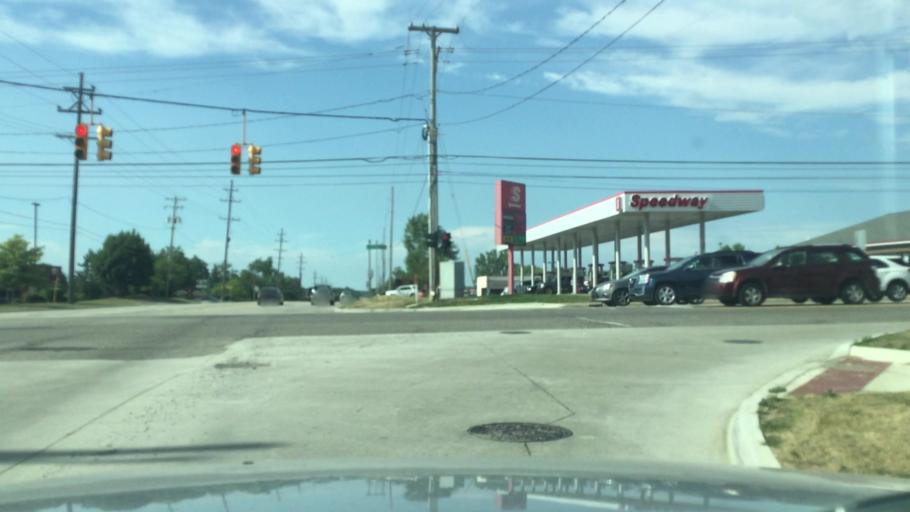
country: US
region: Michigan
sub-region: Genesee County
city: Swartz Creek
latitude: 43.0018
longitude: -83.7726
